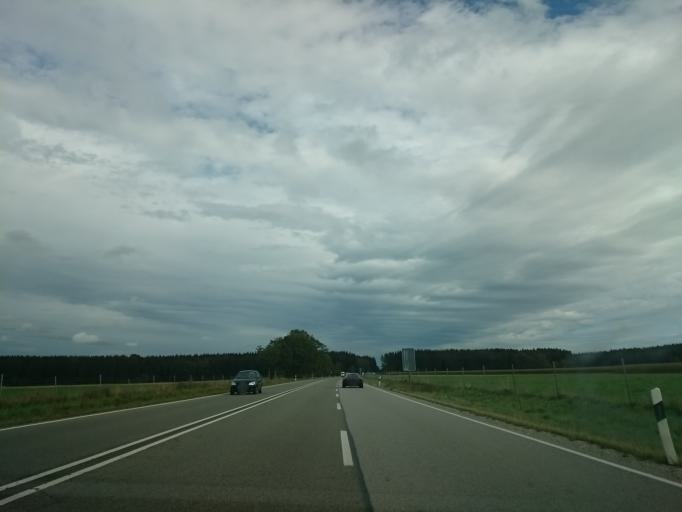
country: DE
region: Bavaria
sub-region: Swabia
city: Jengen
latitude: 47.9758
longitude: 10.6900
